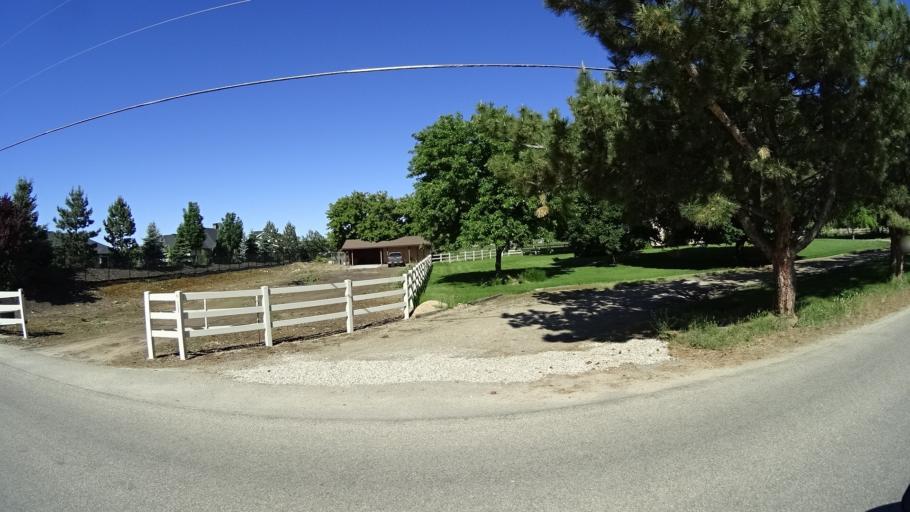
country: US
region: Idaho
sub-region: Ada County
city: Eagle
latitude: 43.6702
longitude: -116.3936
